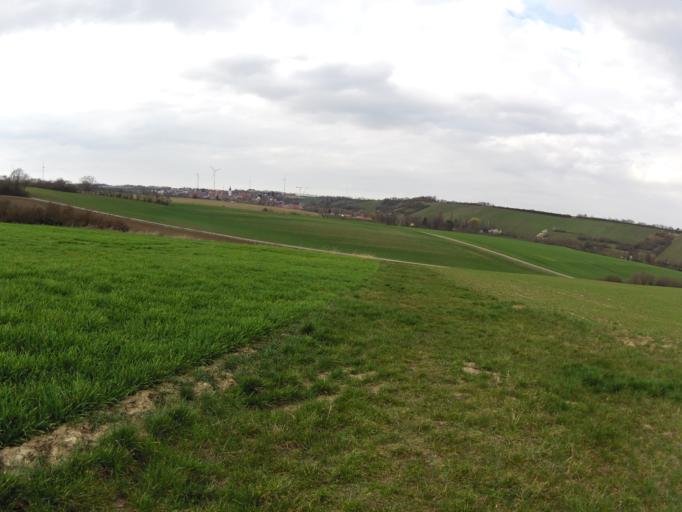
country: DE
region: Bavaria
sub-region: Regierungsbezirk Unterfranken
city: Buchbrunn
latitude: 49.7405
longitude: 10.1300
